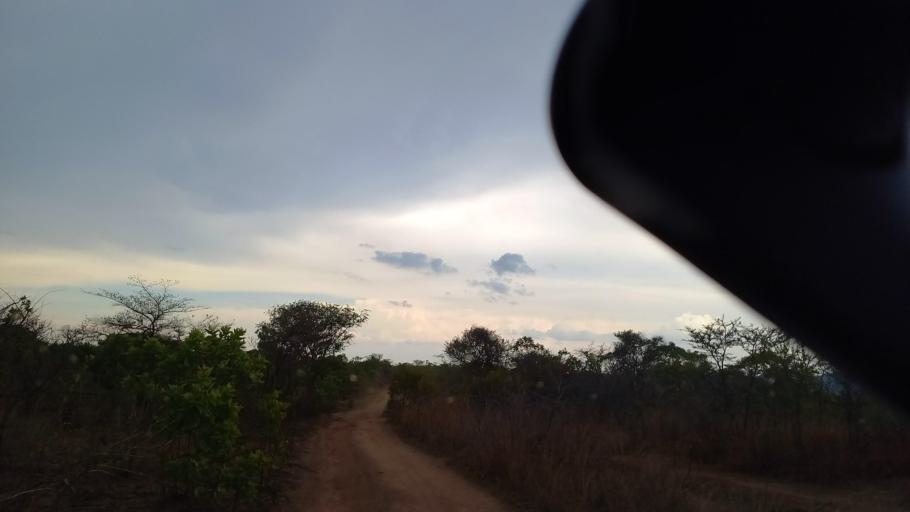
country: ZM
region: Lusaka
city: Kafue
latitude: -15.9954
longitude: 28.2753
